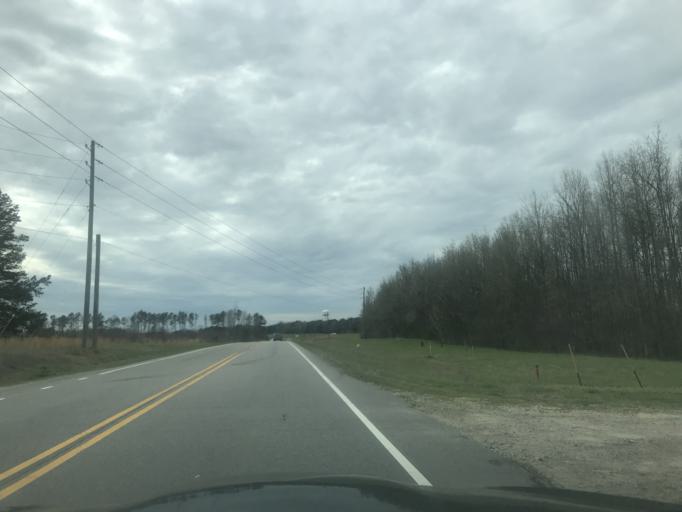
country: US
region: North Carolina
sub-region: Franklin County
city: Franklinton
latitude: 36.0917
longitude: -78.3992
